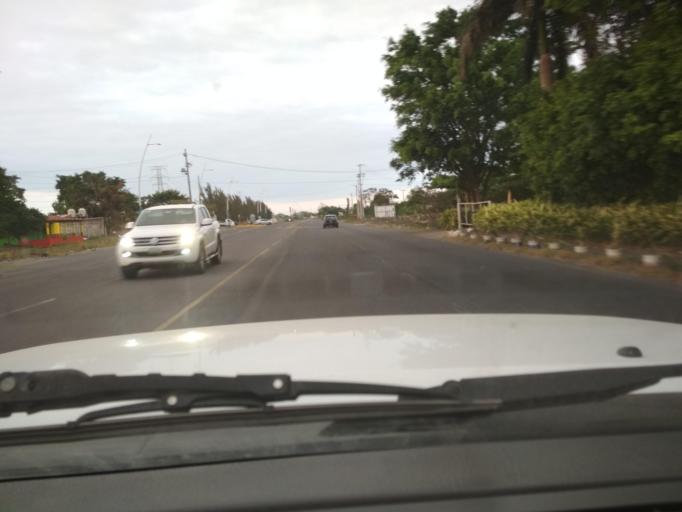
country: MX
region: Veracruz
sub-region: Medellin
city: Fraccionamiento Arboledas San Ramon
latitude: 19.0910
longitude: -96.1532
